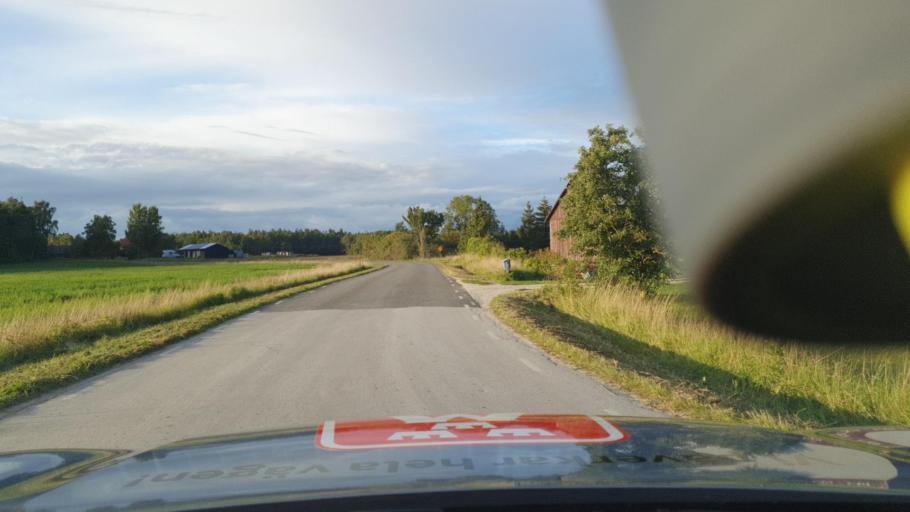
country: SE
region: Gotland
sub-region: Gotland
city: Vibble
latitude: 57.4830
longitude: 18.3366
